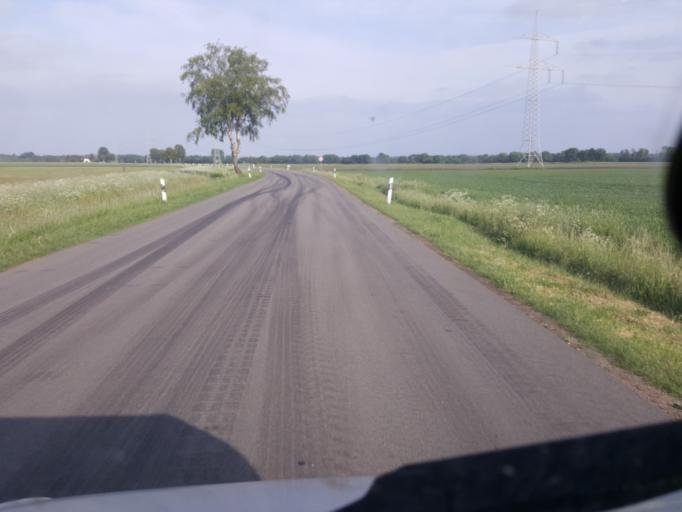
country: DE
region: Lower Saxony
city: Uchte
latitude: 52.5482
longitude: 8.9453
